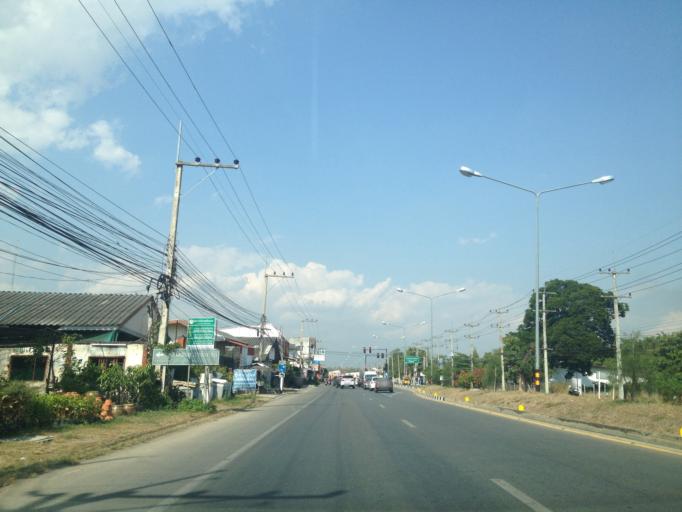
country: TH
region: Chiang Mai
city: San Pa Tong
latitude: 18.5941
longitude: 98.8890
